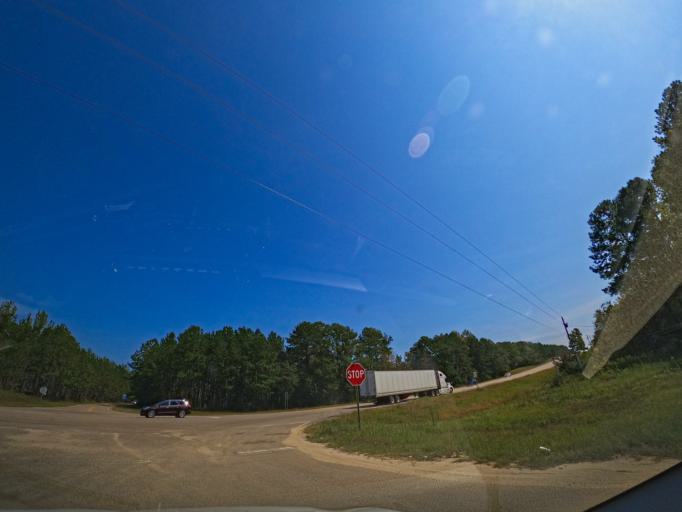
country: US
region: Alabama
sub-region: Butler County
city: Georgiana
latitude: 31.4873
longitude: -86.6825
